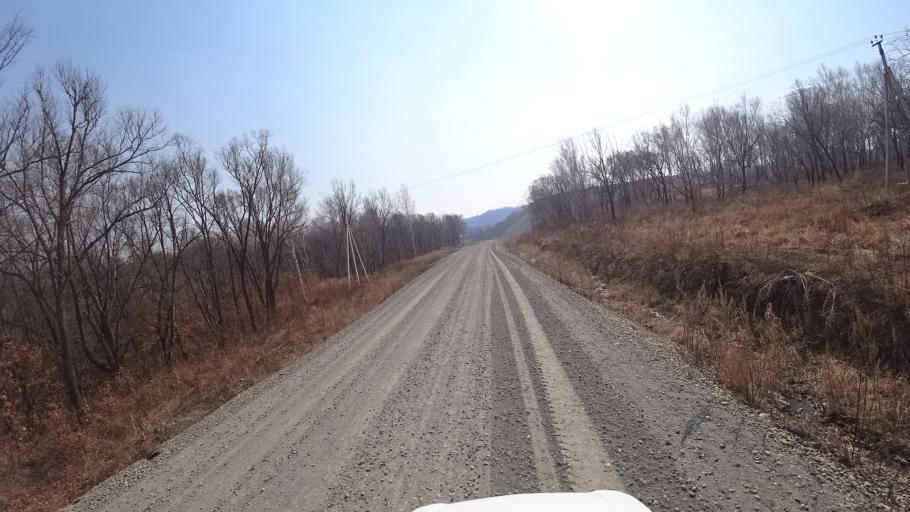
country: RU
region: Amur
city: Novobureyskiy
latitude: 49.8009
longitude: 129.9600
